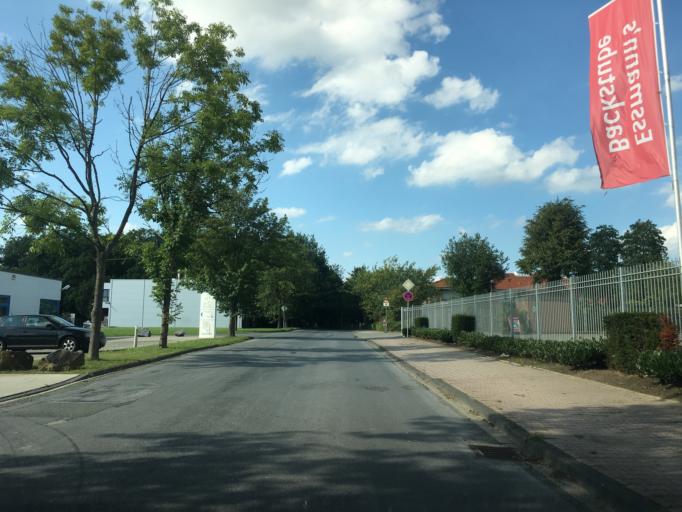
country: DE
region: North Rhine-Westphalia
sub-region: Regierungsbezirk Munster
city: Altenberge
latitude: 52.0370
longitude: 7.4527
